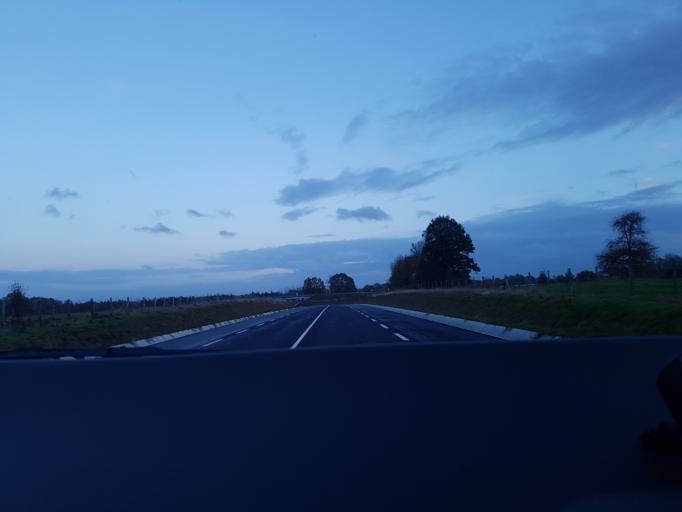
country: FR
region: Haute-Normandie
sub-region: Departement de l'Eure
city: Beuzeville
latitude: 49.3276
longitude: 0.3219
